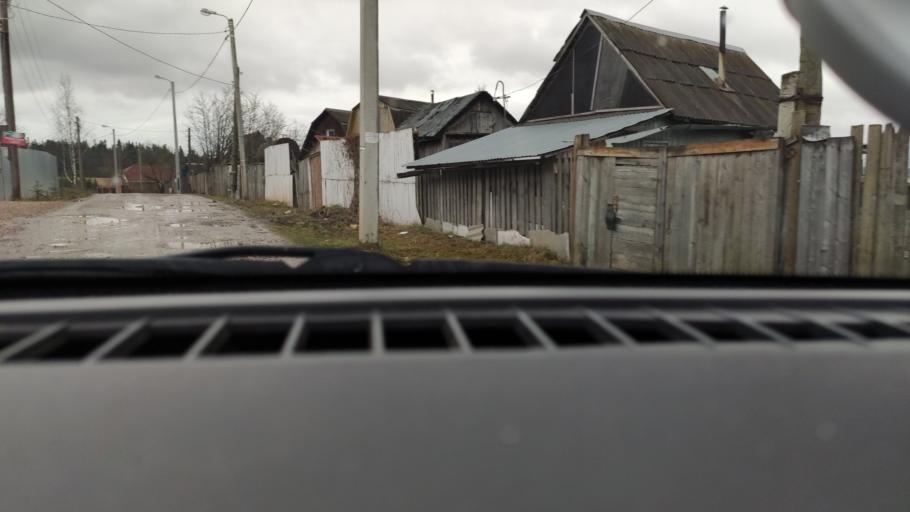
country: RU
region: Perm
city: Froly
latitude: 57.9468
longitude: 56.3046
